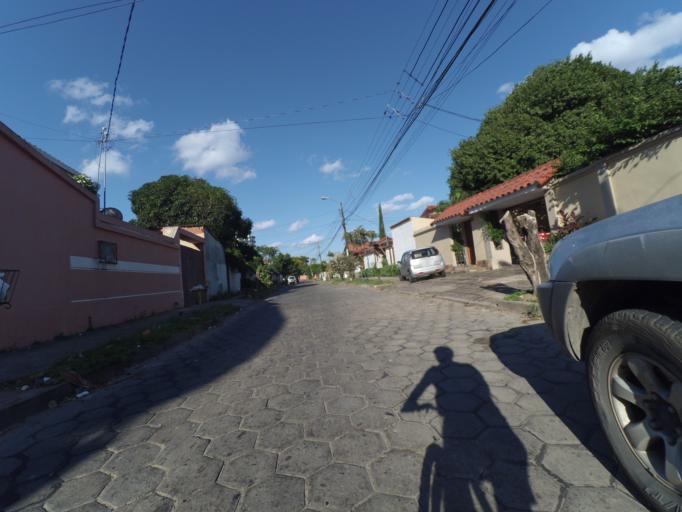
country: BO
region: Santa Cruz
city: Santa Cruz de la Sierra
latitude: -17.8012
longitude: -63.1987
